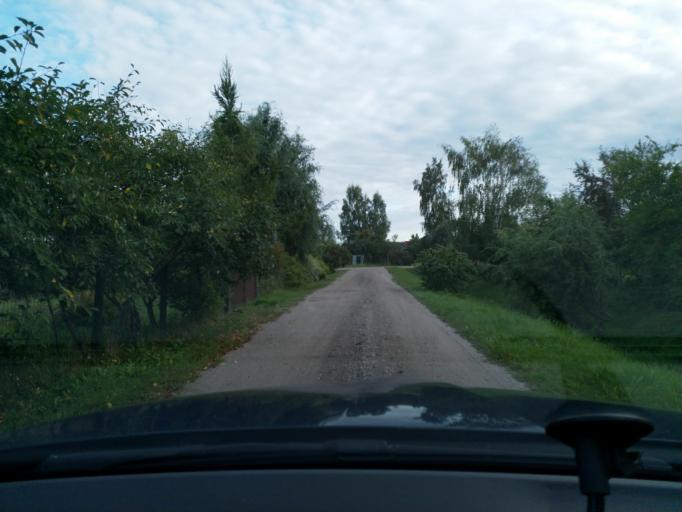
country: LV
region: Kuldigas Rajons
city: Kuldiga
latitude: 56.9523
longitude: 21.9770
